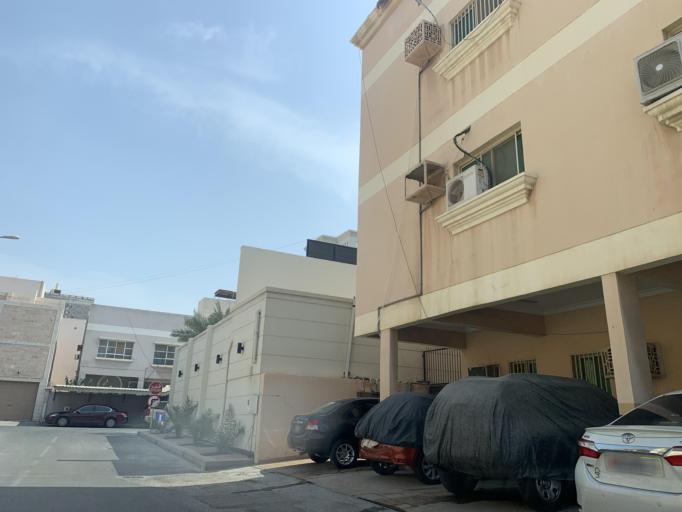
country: BH
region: Muharraq
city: Al Hadd
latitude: 26.2676
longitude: 50.6544
